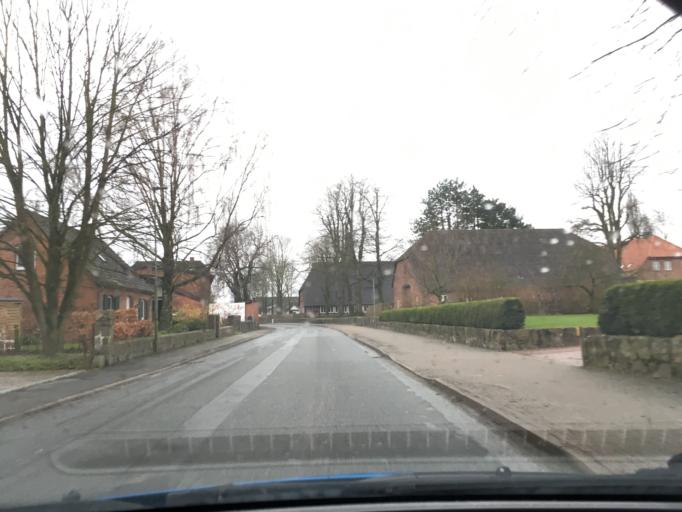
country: DE
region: Schleswig-Holstein
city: Breitenfelde
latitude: 53.6040
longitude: 10.6394
